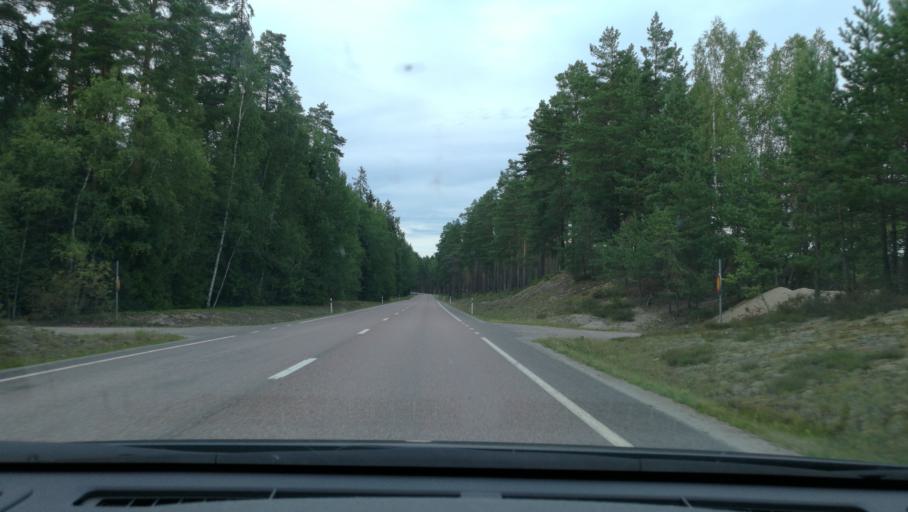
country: SE
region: Vaestmanland
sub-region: Kungsors Kommun
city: Kungsoer
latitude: 59.3835
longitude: 16.1087
